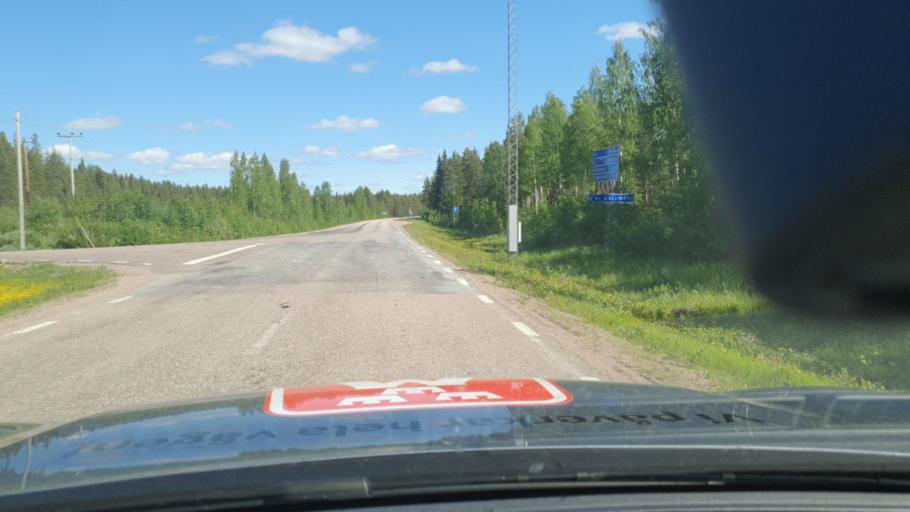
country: SE
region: Norrbotten
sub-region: Overkalix Kommun
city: OEverkalix
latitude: 67.0705
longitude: 22.5217
